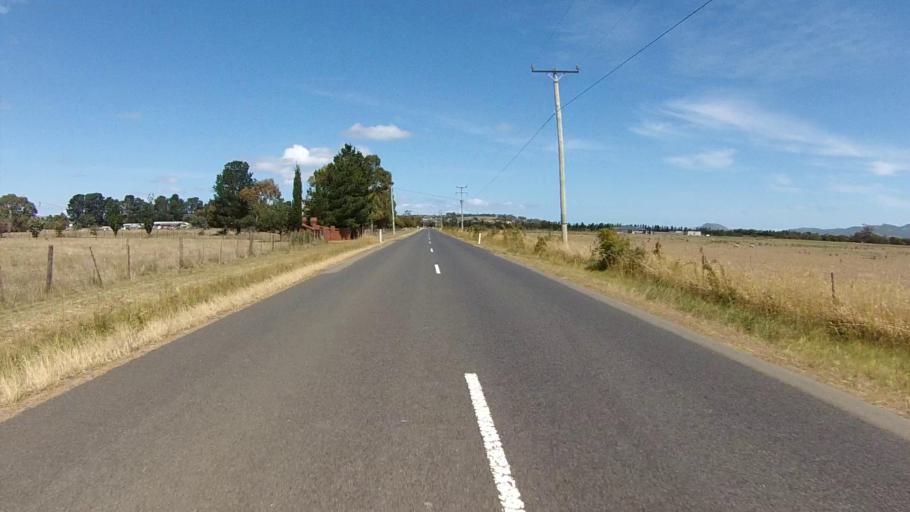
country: AU
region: Tasmania
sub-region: Sorell
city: Sorell
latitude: -42.7729
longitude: 147.5184
